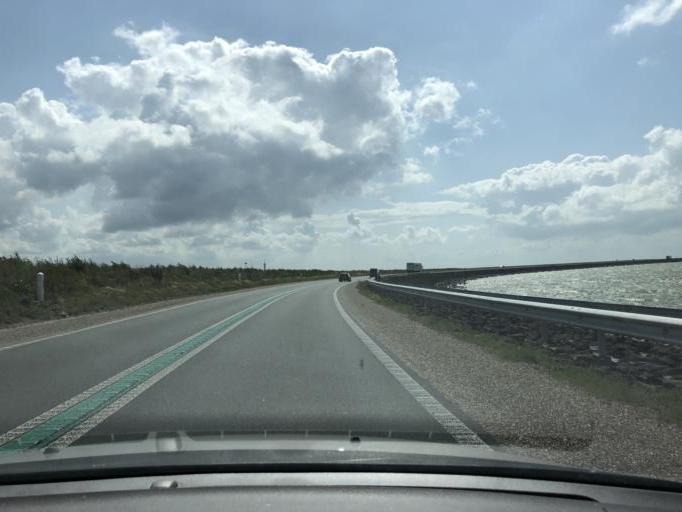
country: NL
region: Flevoland
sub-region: Gemeente Lelystad
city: Lelystad
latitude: 52.5680
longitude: 5.4670
